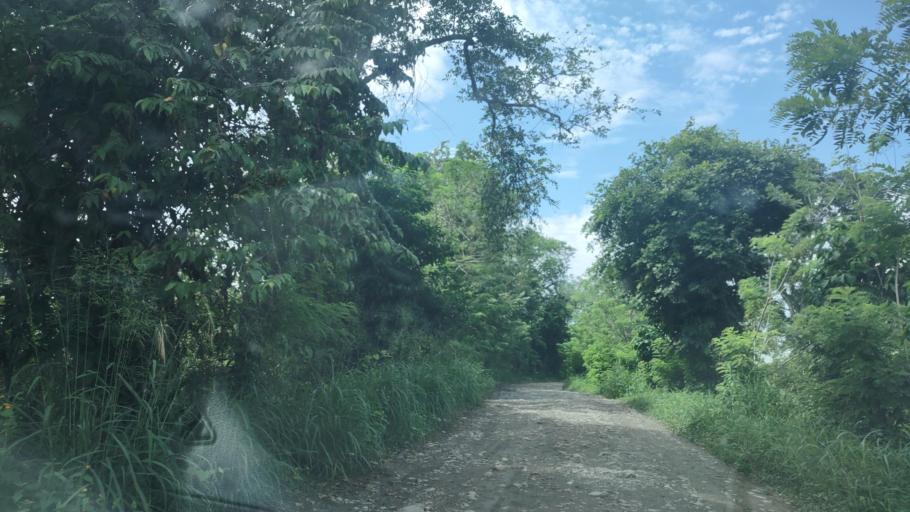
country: MX
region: Veracruz
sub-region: Atzalan
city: Colonias Pedernales
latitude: 20.0565
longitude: -97.0133
